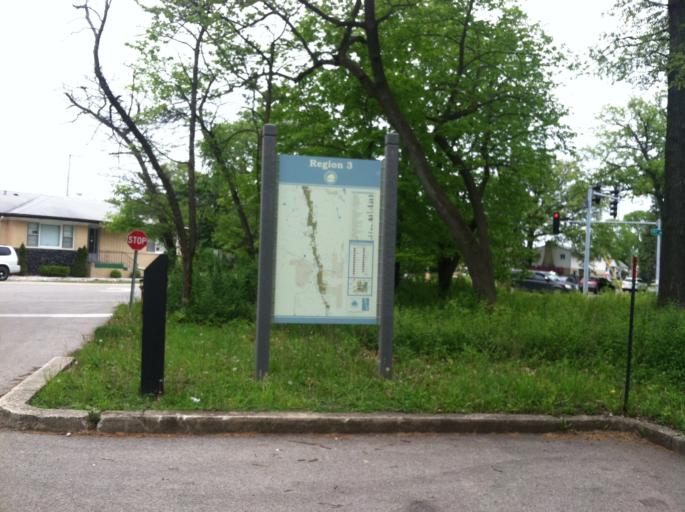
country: US
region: Illinois
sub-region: Cook County
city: River Grove
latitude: 41.9228
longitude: -87.8361
